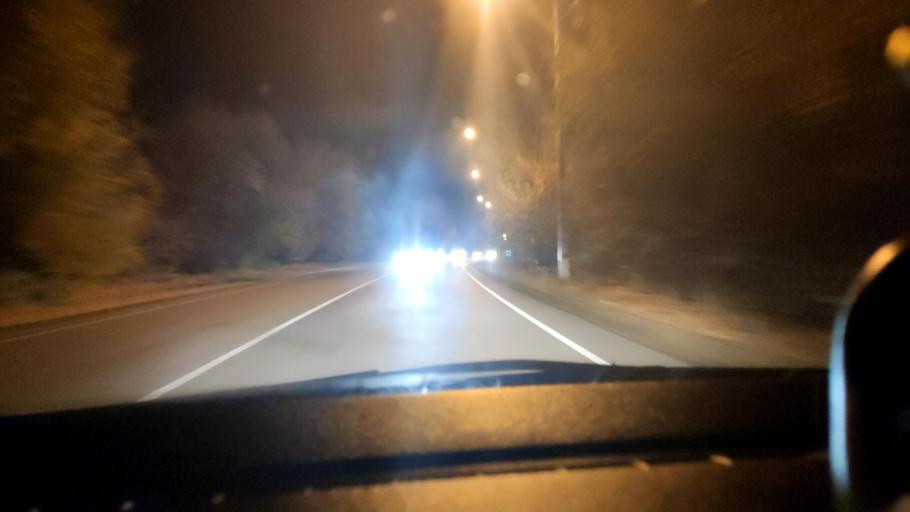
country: RU
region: Voronezj
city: Maslovka
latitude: 51.5955
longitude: 39.1769
